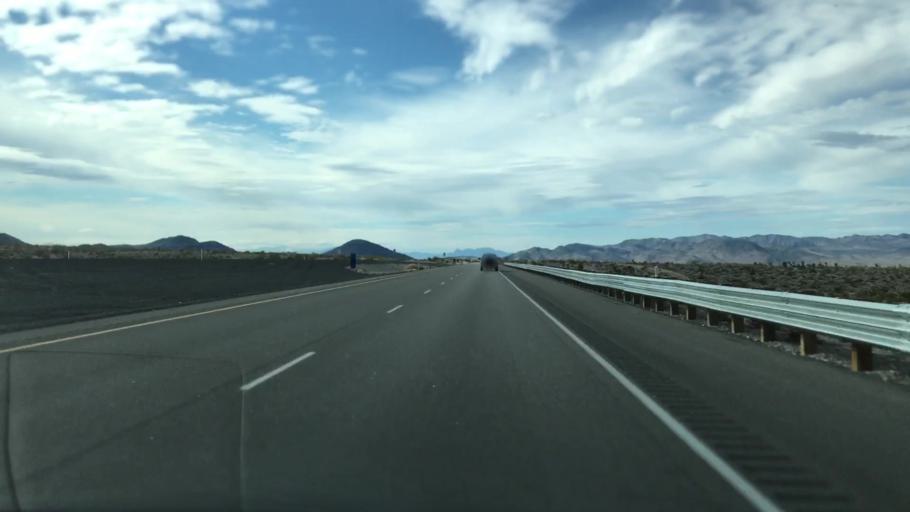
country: US
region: Nevada
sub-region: Nye County
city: Pahrump
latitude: 36.6009
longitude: -115.9869
